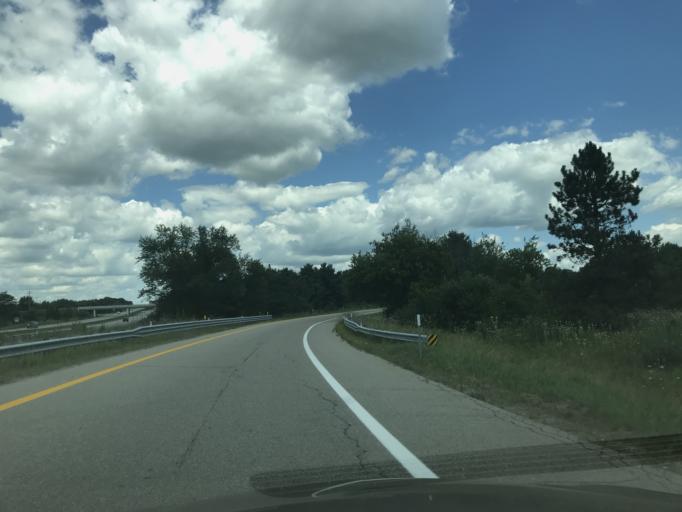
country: US
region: Michigan
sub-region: Ingham County
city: Leslie
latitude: 42.4477
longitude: -84.4433
